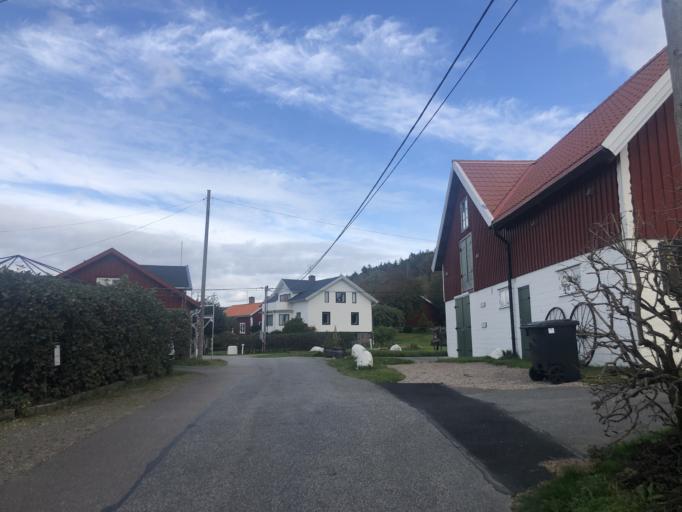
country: SE
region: Vaestra Goetaland
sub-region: Molndal
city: Moelndal
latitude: 57.6502
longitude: 11.9785
